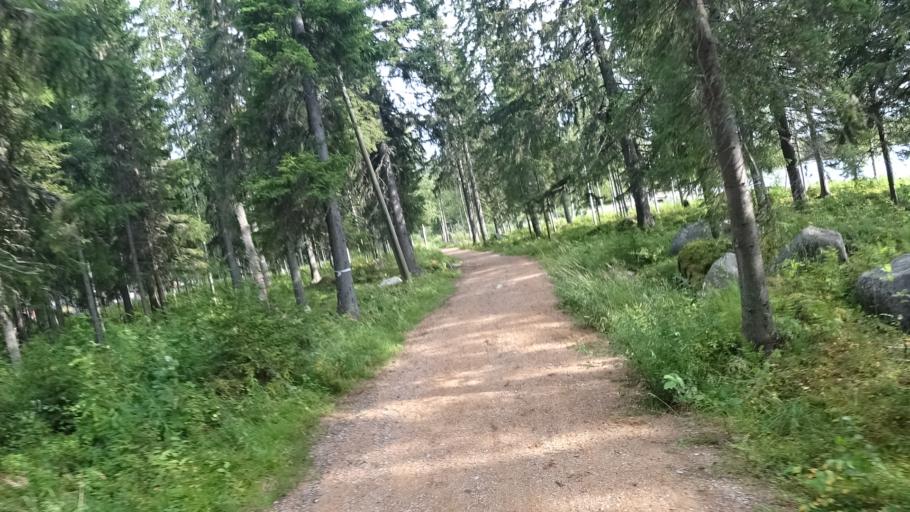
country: FI
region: North Karelia
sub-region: Joensuu
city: Ilomantsi
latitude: 62.6671
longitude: 30.9107
